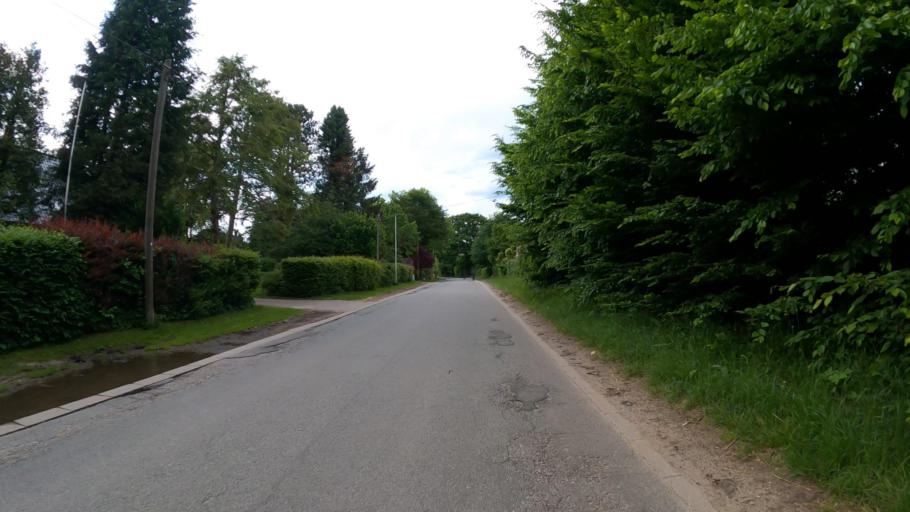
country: DE
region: Schleswig-Holstein
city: Rellingen
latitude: 53.6118
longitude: 9.7953
